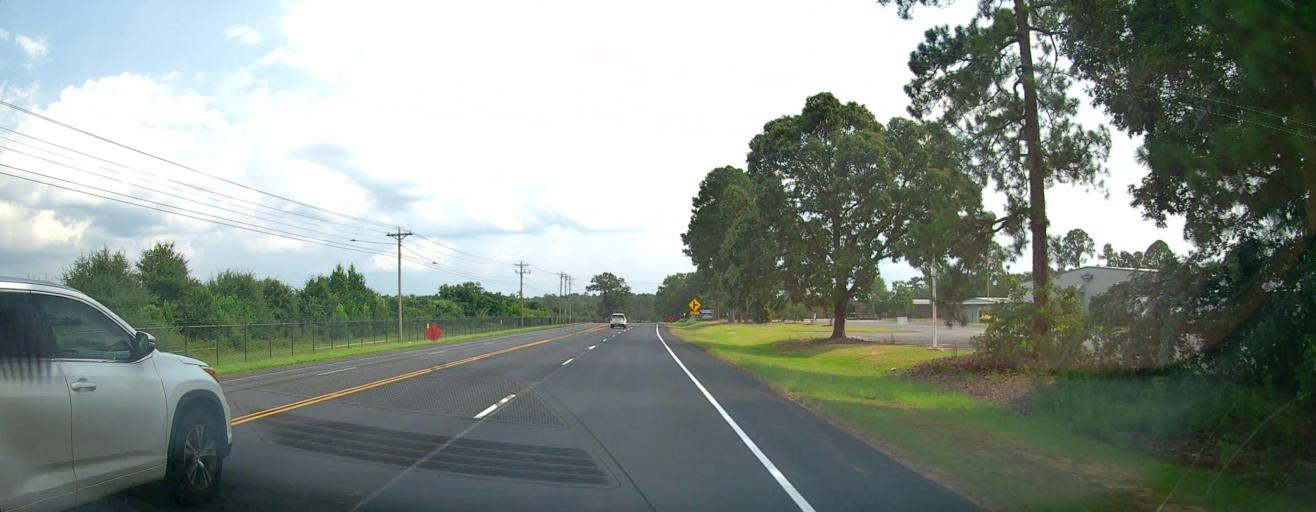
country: US
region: Georgia
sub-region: Houston County
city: Robins Air Force Base
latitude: 32.5851
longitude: -83.5873
